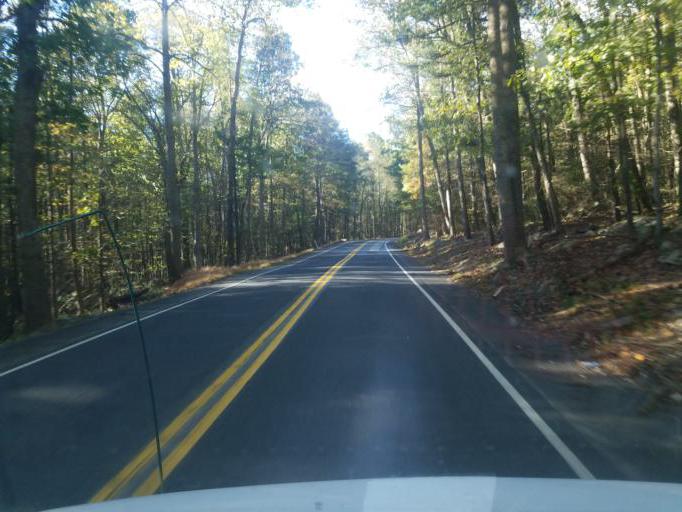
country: US
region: Pennsylvania
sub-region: Franklin County
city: Mont Alto
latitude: 39.8660
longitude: -77.4988
